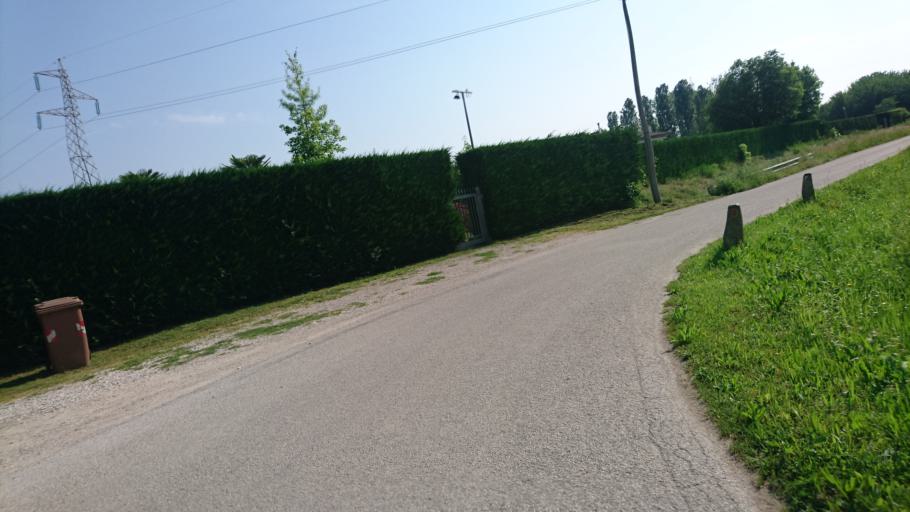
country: IT
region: Veneto
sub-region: Provincia di Padova
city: Saonara
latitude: 45.3670
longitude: 11.9698
